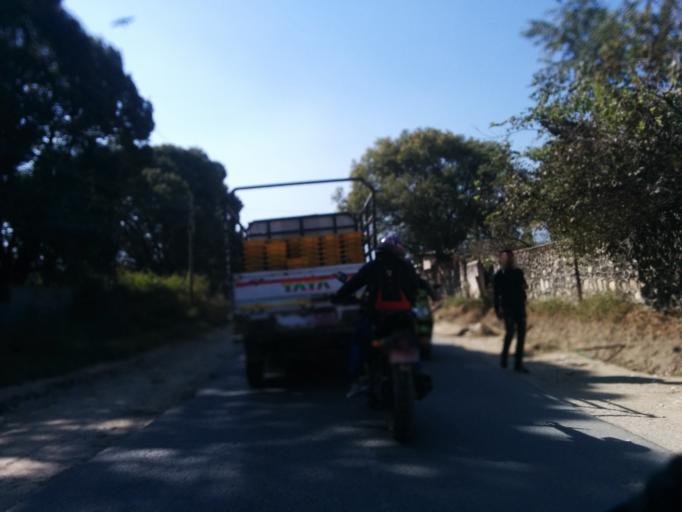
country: NP
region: Central Region
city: Kirtipur
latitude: 27.6774
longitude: 85.2843
